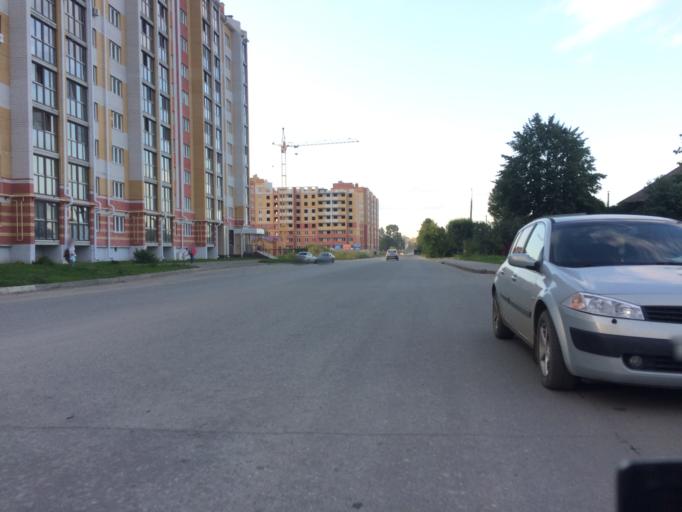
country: RU
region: Mariy-El
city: Medvedevo
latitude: 56.6482
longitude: 47.8362
